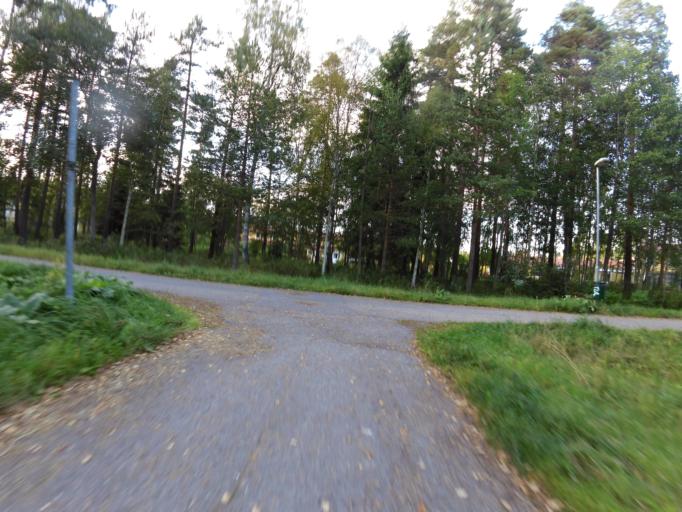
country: SE
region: Gaevleborg
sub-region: Gavle Kommun
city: Gavle
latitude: 60.6634
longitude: 17.2374
